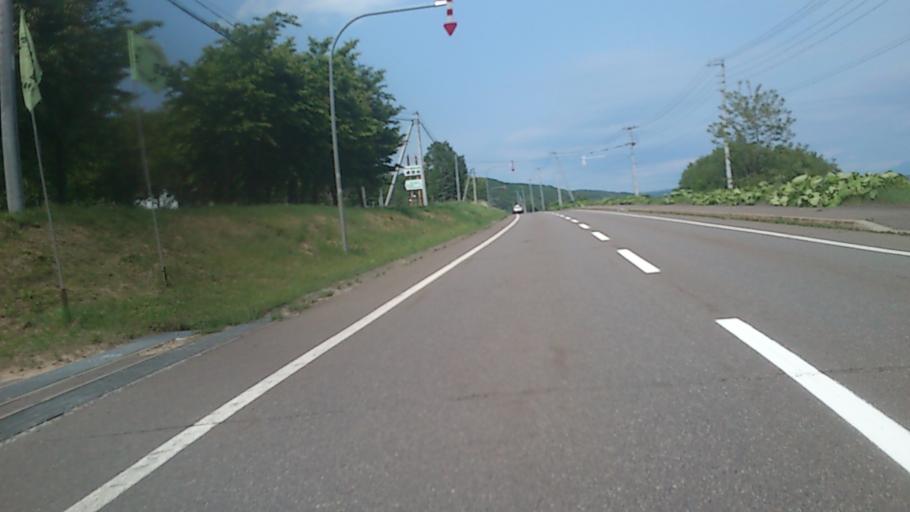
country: JP
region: Hokkaido
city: Otofuke
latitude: 43.2560
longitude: 143.5693
